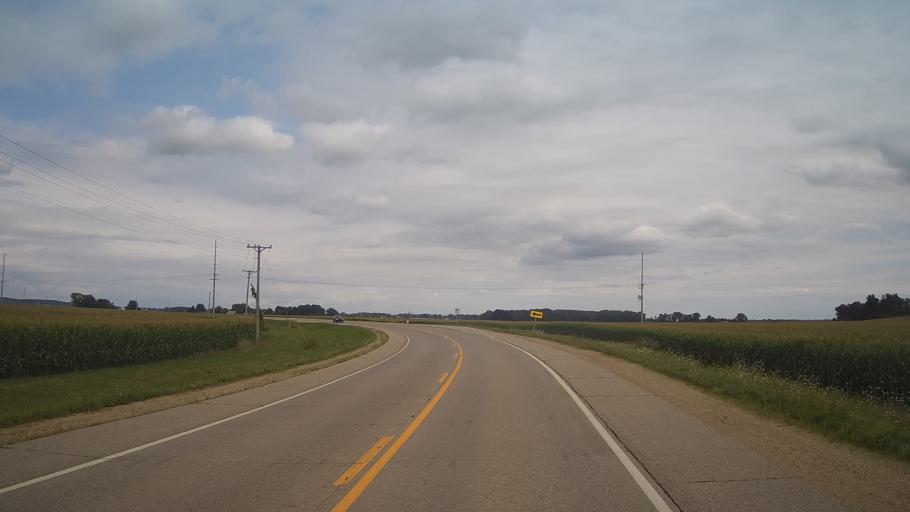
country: US
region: Wisconsin
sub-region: Waushara County
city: Redgranite
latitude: 44.0376
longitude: -89.0490
